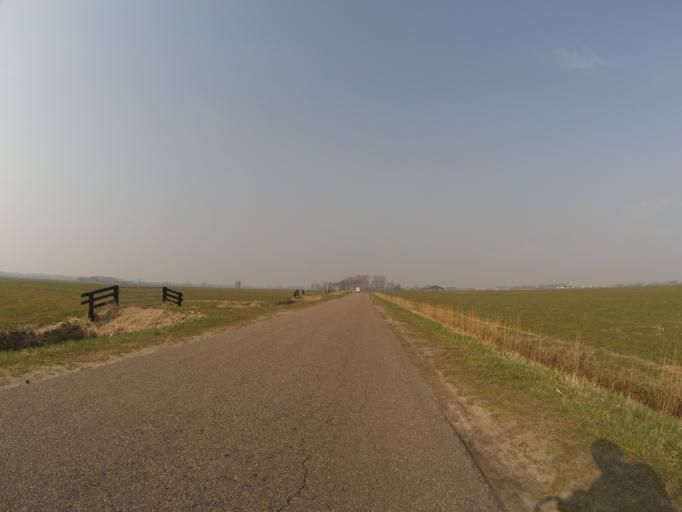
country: NL
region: Utrecht
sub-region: Gemeente Amersfoort
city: Hoogland
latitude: 52.1973
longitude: 5.3337
